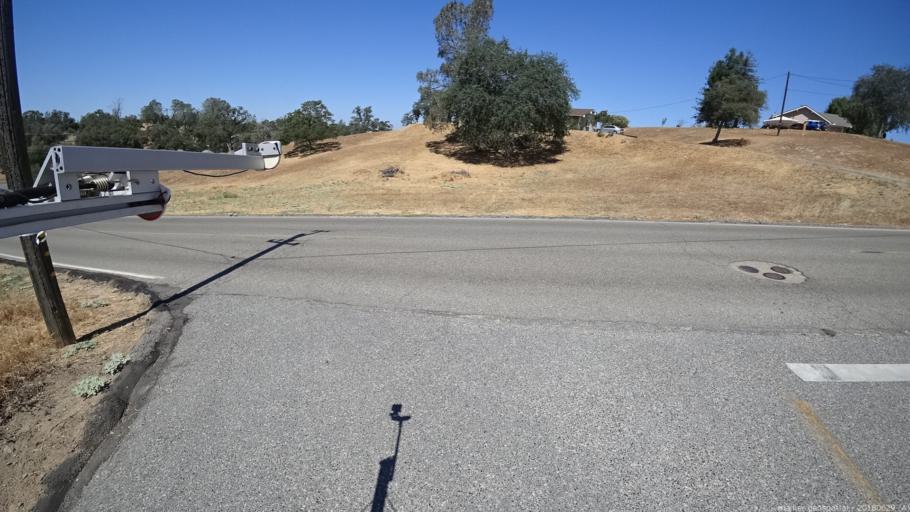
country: US
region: California
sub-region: Madera County
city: Yosemite Lakes
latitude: 37.1704
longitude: -119.7555
